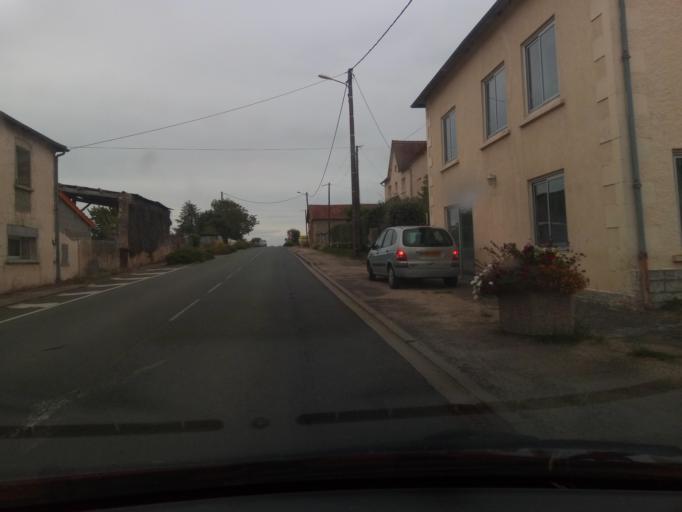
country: FR
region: Poitou-Charentes
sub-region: Departement de la Vienne
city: Saint-Savin
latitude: 46.5049
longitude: 0.7762
